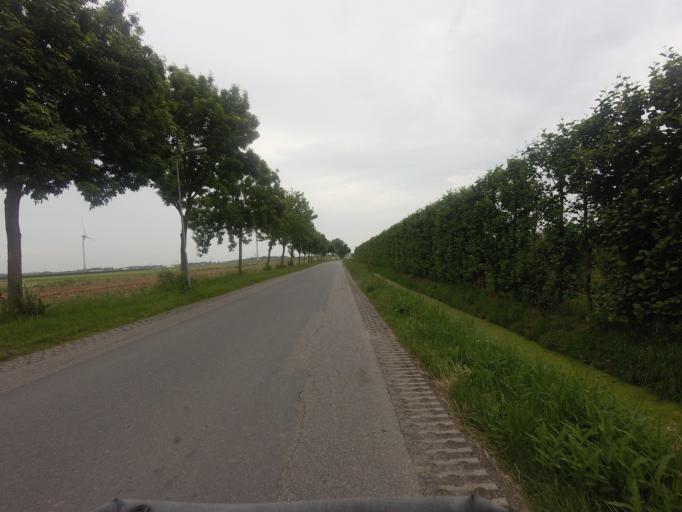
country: NL
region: North Holland
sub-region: Gemeente Hoorn
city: Hoorn
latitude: 52.6884
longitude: 5.1271
